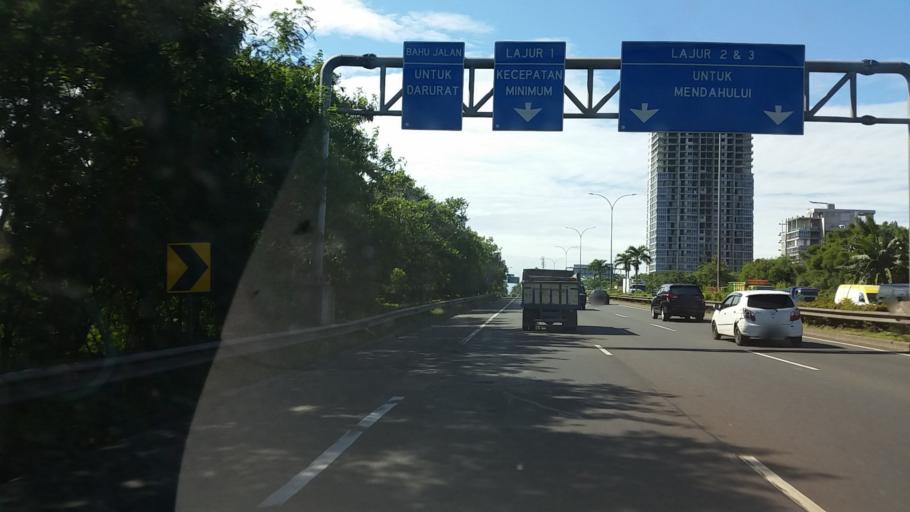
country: ID
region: Banten
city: South Tangerang
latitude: -6.2706
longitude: 106.7683
